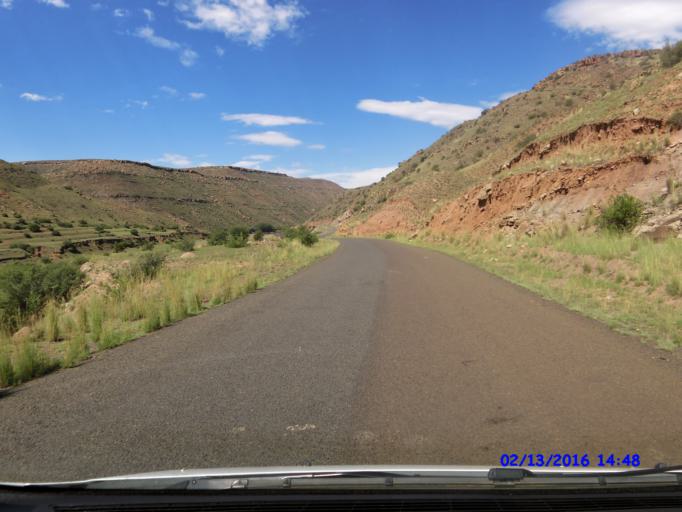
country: LS
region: Qacha's Nek
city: Qacha's Nek
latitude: -30.0682
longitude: 28.4173
